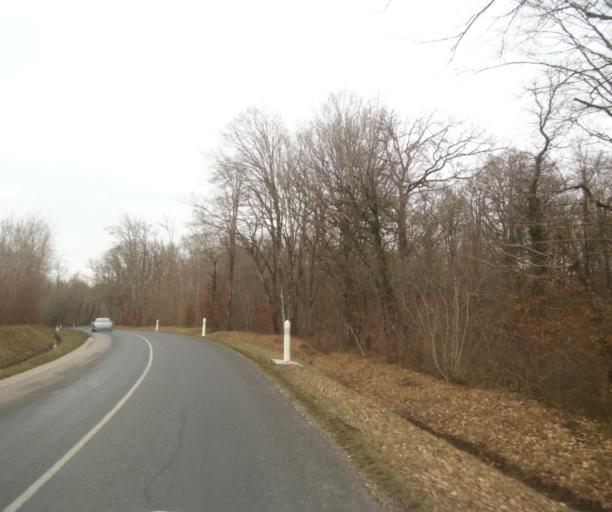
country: FR
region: Champagne-Ardenne
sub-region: Departement de la Marne
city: Pargny-sur-Saulx
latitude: 48.7297
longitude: 4.8665
